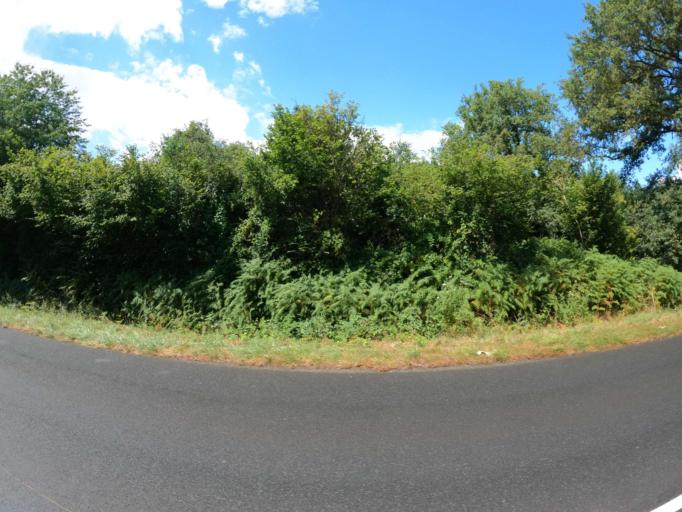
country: FR
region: Pays de la Loire
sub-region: Departement de Maine-et-Loire
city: Feneu
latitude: 47.5967
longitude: -0.5884
